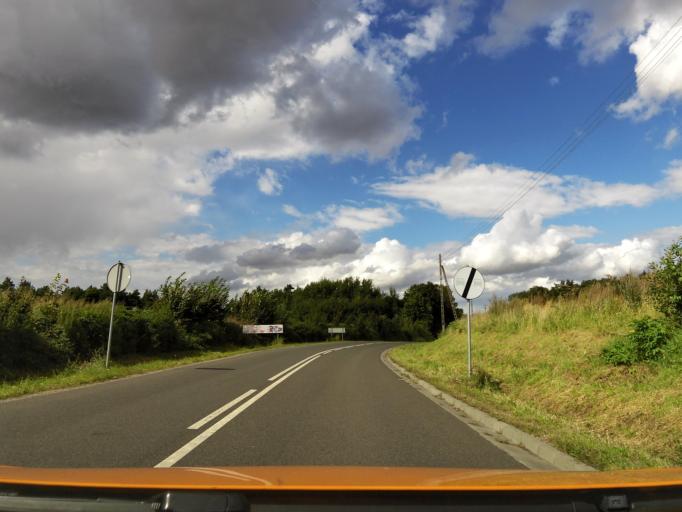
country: PL
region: West Pomeranian Voivodeship
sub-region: Powiat kolobrzeski
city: Ryman
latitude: 53.9781
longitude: 15.4888
